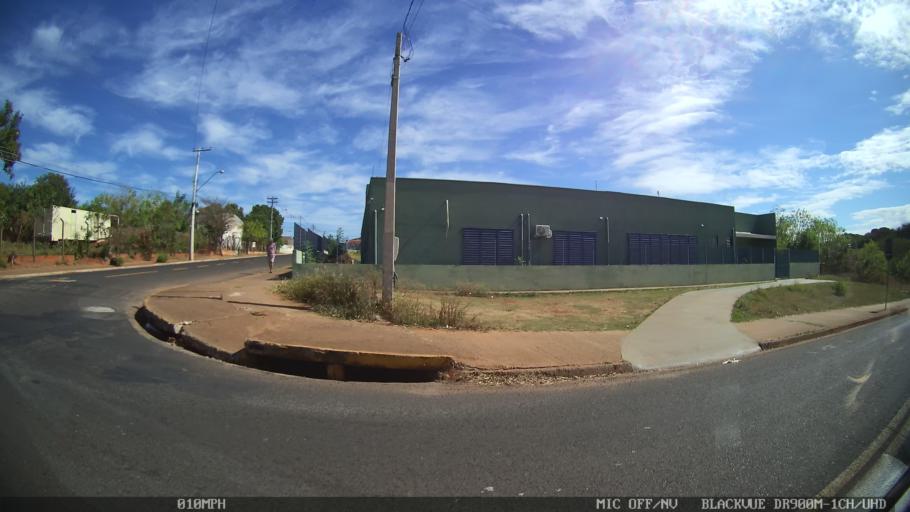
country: BR
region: Sao Paulo
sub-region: Bady Bassitt
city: Bady Bassitt
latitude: -20.8270
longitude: -49.4944
